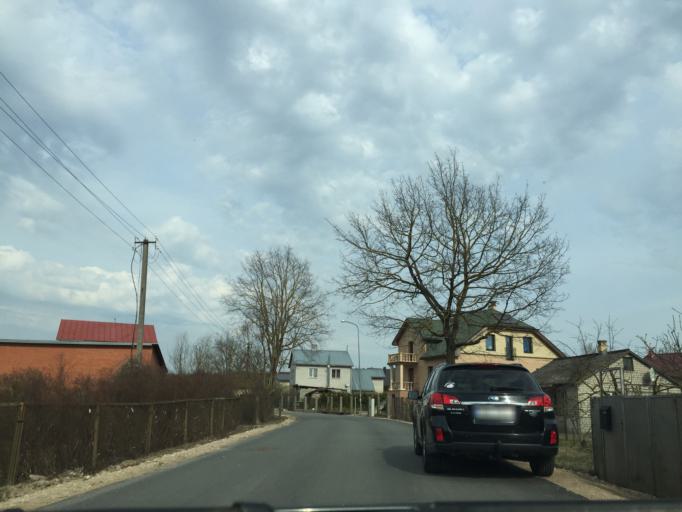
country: LV
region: Kekava
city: Balozi
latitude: 56.8786
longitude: 24.1532
